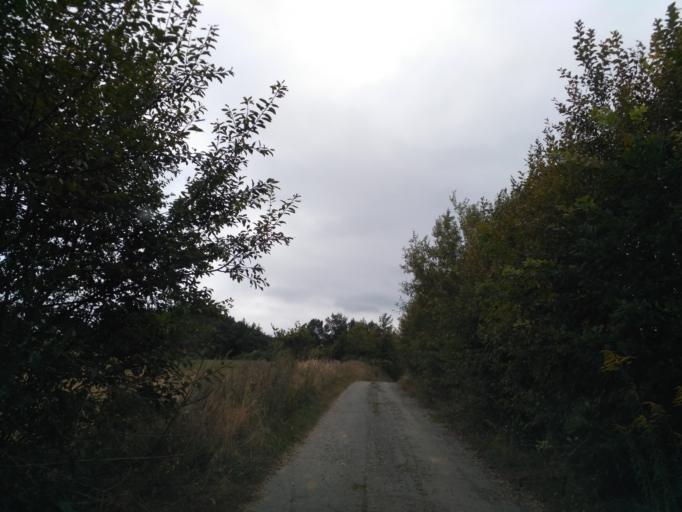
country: SK
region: Presovsky
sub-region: Okres Presov
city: Presov
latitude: 48.9208
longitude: 21.1826
